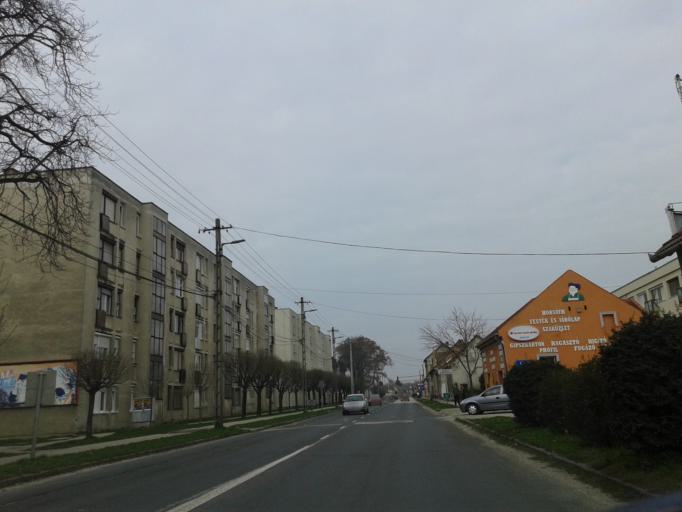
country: HU
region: Komarom-Esztergom
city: Komarom
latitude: 47.7457
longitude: 18.1124
